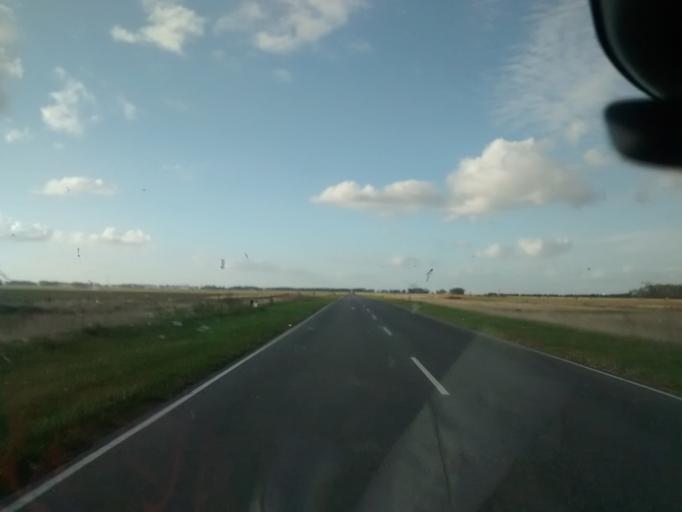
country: AR
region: Buenos Aires
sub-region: Partido de General Belgrano
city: General Belgrano
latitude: -36.1839
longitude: -58.5934
